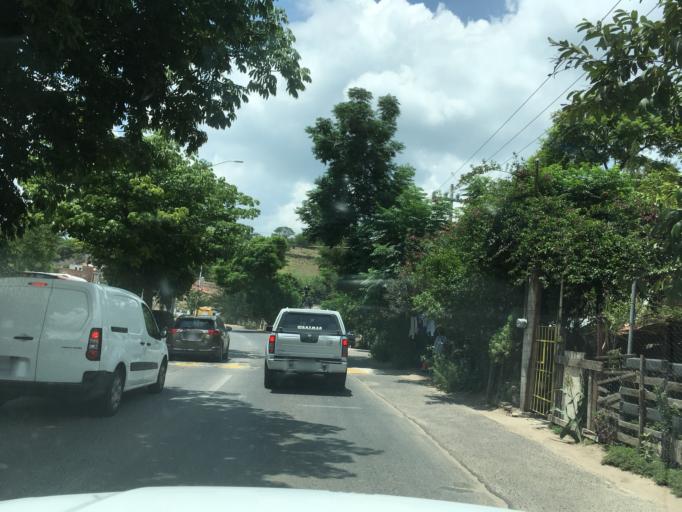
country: MX
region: Jalisco
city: Tlajomulco de Zuniga
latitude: 20.4691
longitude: -103.4523
